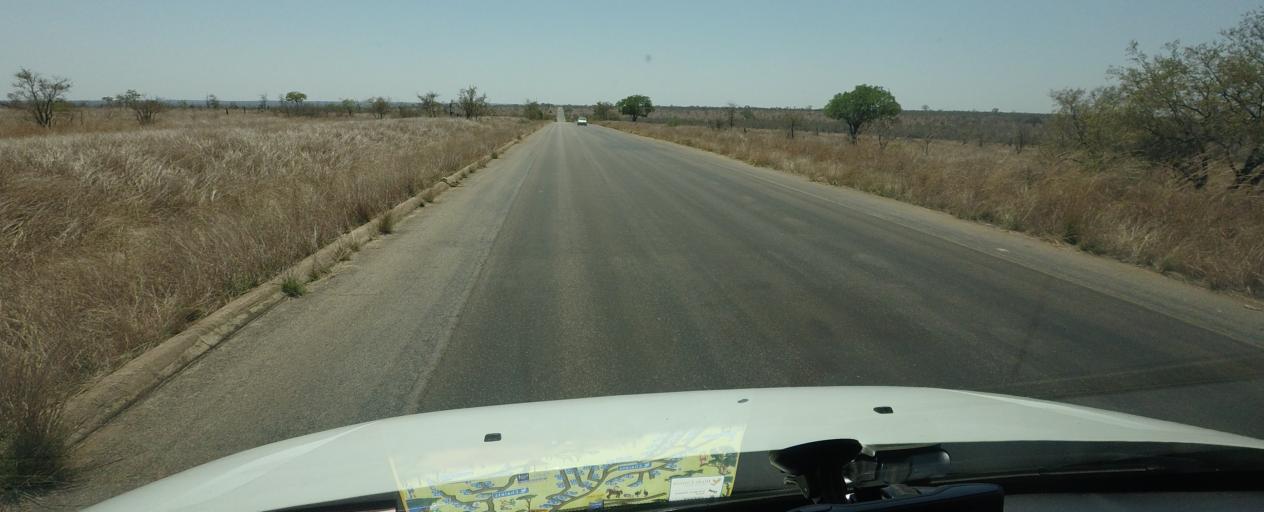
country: ZA
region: Limpopo
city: Thulamahashi
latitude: -24.4978
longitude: 31.3831
